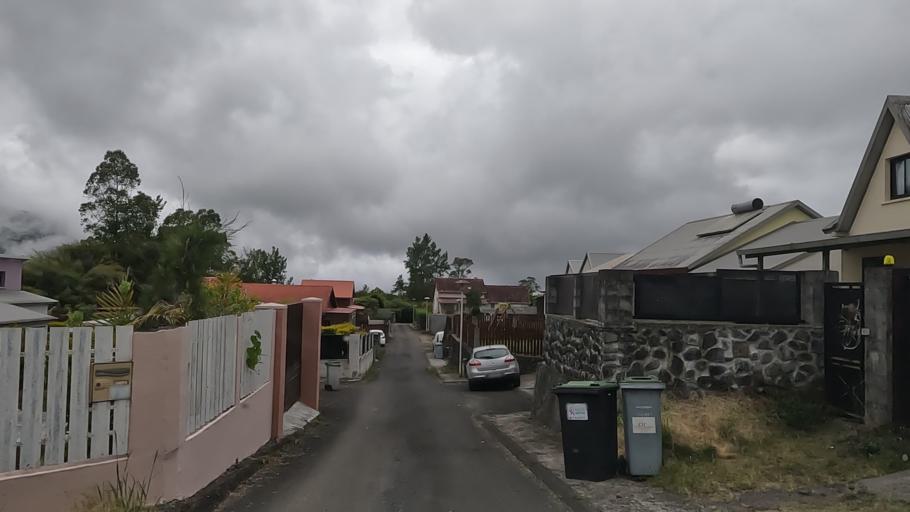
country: RE
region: Reunion
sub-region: Reunion
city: Saint-Benoit
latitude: -21.1396
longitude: 55.6257
